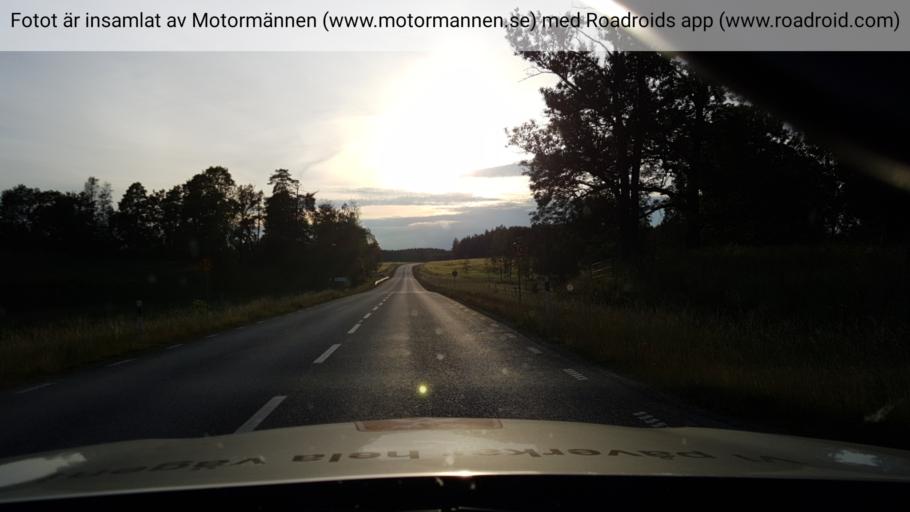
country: SE
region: OErebro
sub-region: Lindesbergs Kommun
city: Lindesberg
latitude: 59.5280
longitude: 15.2807
